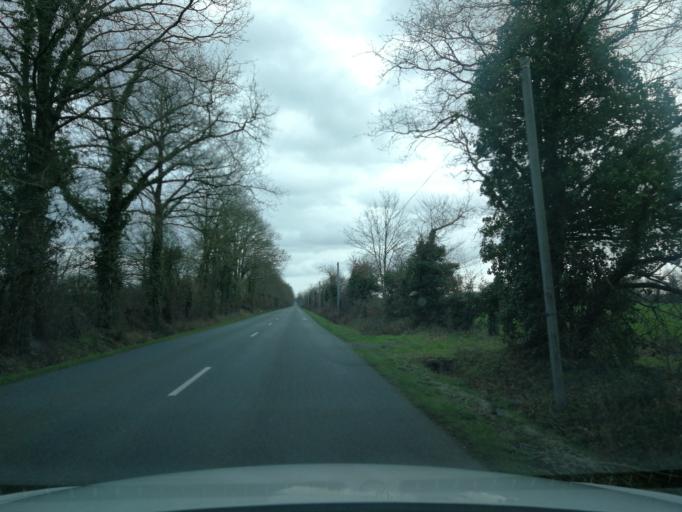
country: FR
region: Pays de la Loire
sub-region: Departement de la Loire-Atlantique
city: Geneston
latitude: 47.0319
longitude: -1.5011
